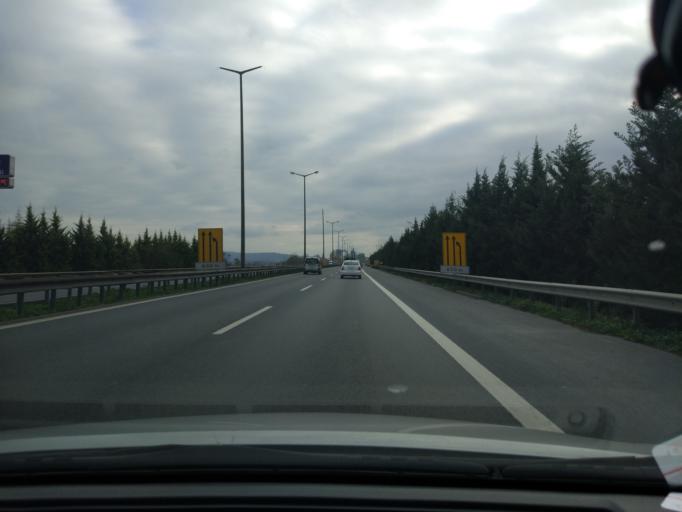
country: TR
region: Kocaeli
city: Kosekoy
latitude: 40.7678
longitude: 30.0148
